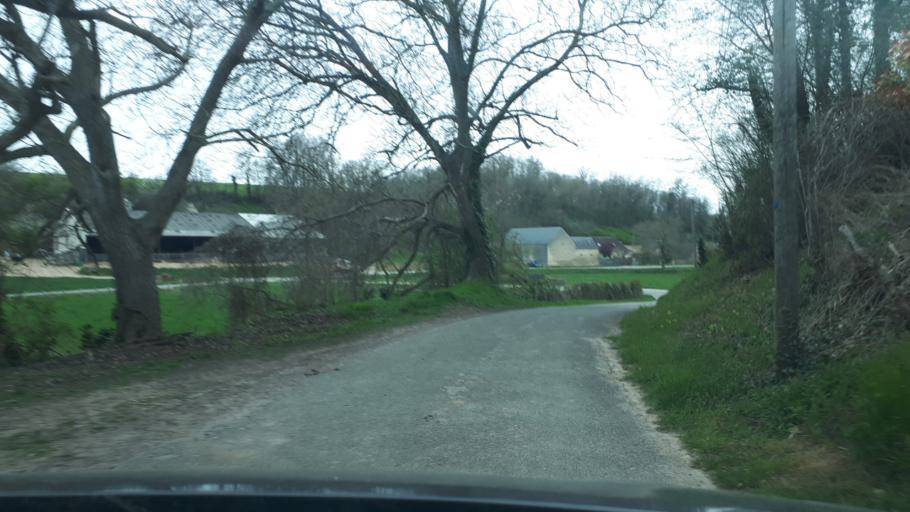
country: FR
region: Centre
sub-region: Departement du Loir-et-Cher
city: Lunay
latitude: 47.7550
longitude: 0.9291
